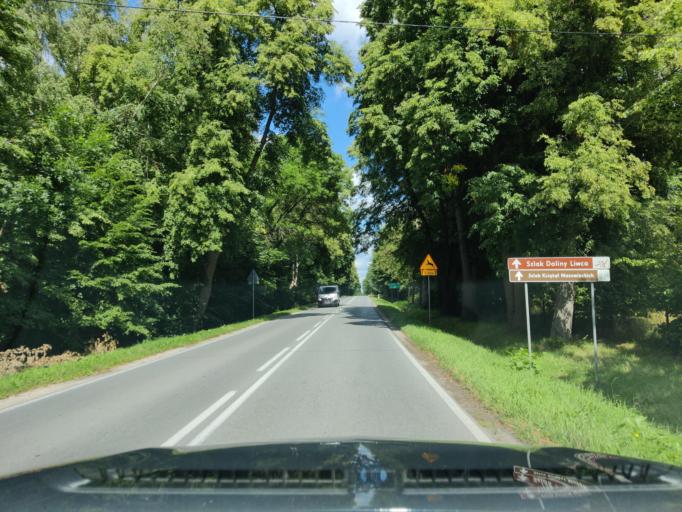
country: PL
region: Masovian Voivodeship
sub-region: Powiat minski
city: Kaluszyn
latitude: 52.2107
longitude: 21.8623
